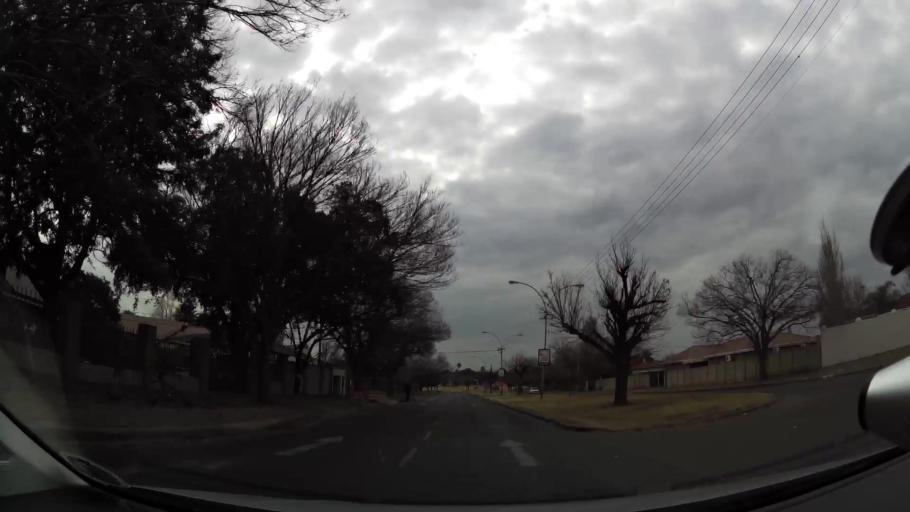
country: ZA
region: Orange Free State
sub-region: Mangaung Metropolitan Municipality
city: Bloemfontein
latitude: -29.0906
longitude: 26.2150
